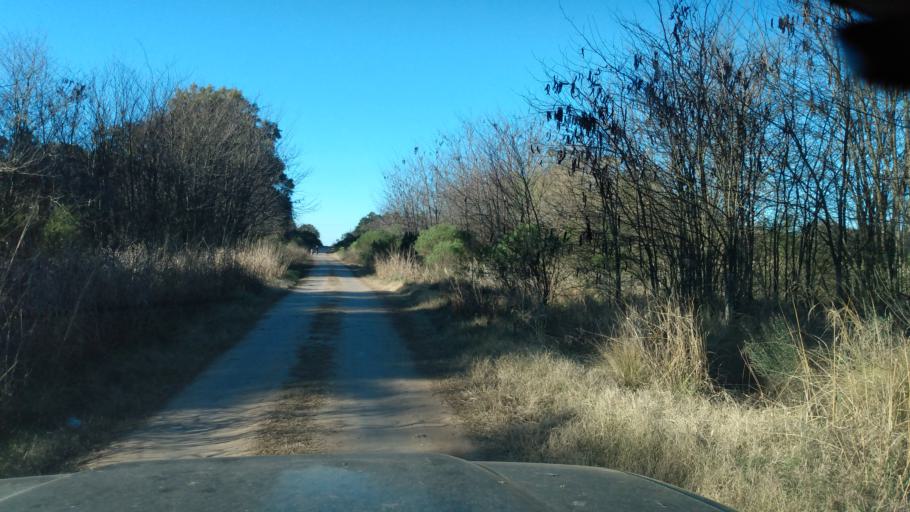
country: AR
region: Buenos Aires
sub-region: Partido de Lujan
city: Lujan
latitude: -34.5576
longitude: -59.1553
